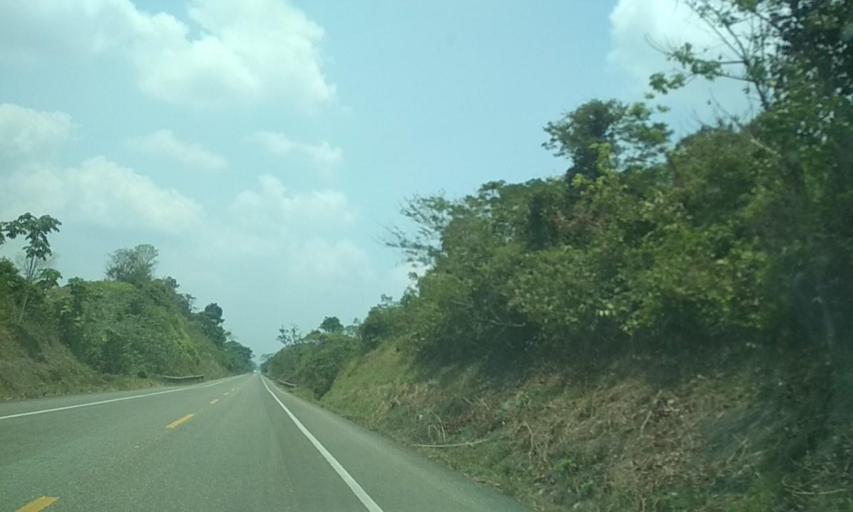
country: MX
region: Tabasco
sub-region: Huimanguillo
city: Francisco Rueda
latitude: 17.6607
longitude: -93.8538
